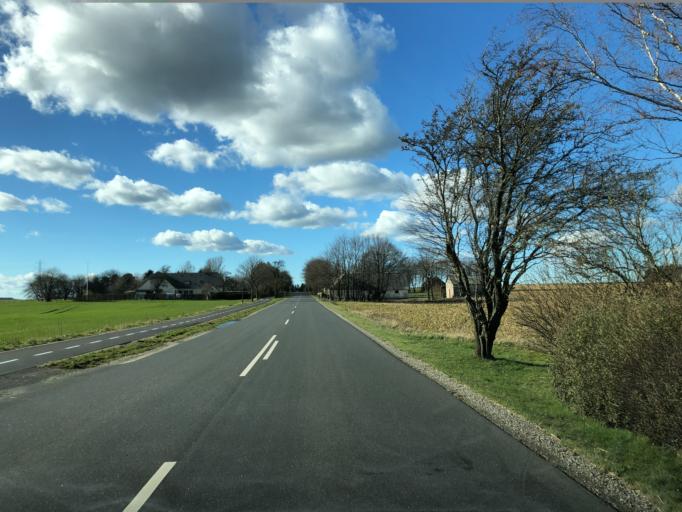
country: DK
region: Central Jutland
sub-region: Favrskov Kommune
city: Hinnerup
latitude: 56.2836
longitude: 10.0243
